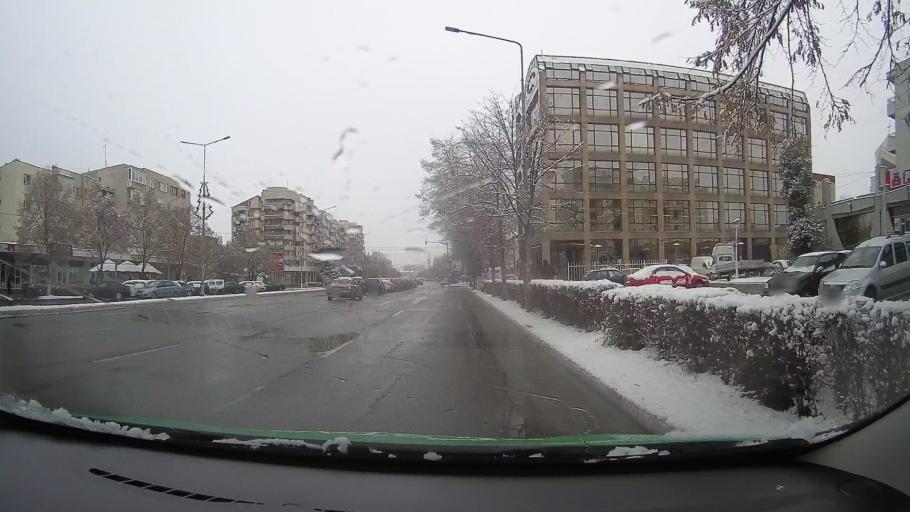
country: RO
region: Hunedoara
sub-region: Municipiul Deva
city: Deva
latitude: 45.8721
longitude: 22.9094
